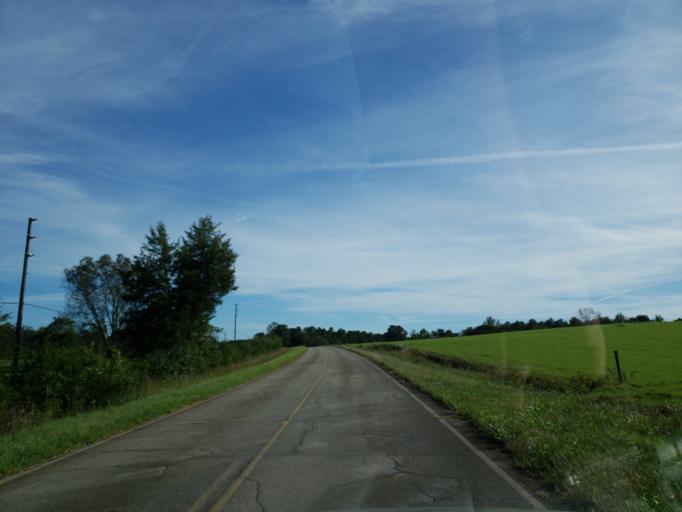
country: US
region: Georgia
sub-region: Crawford County
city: Roberta
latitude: 32.8403
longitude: -84.0775
